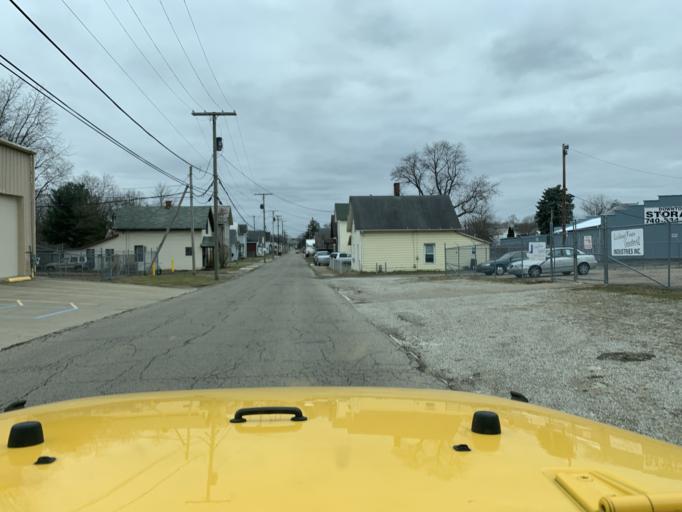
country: US
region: Ohio
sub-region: Licking County
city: Newark
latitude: 40.0549
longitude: -82.4060
